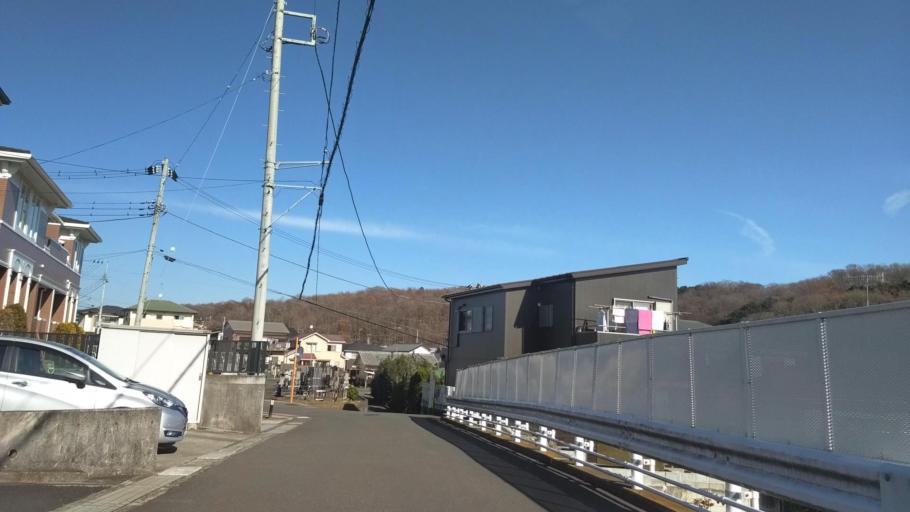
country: JP
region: Kanagawa
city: Hadano
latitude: 35.3420
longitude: 139.2339
